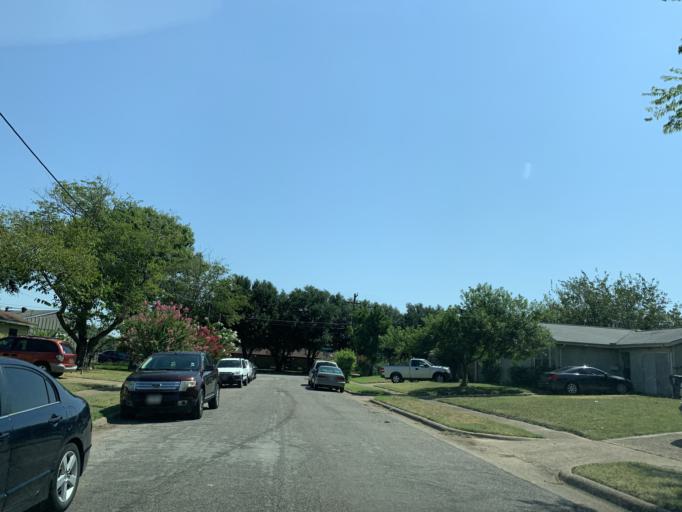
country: US
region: Texas
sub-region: Dallas County
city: Hutchins
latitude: 32.6747
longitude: -96.7576
